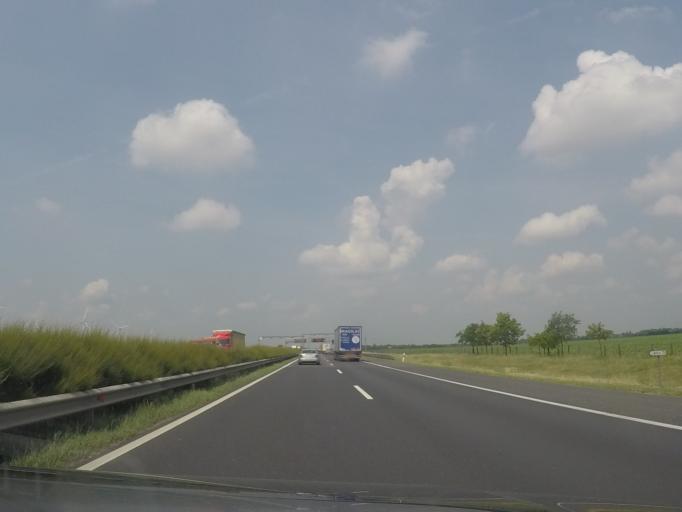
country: HU
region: Gyor-Moson-Sopron
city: Mosonmagyarovar
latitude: 47.8773
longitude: 17.2048
